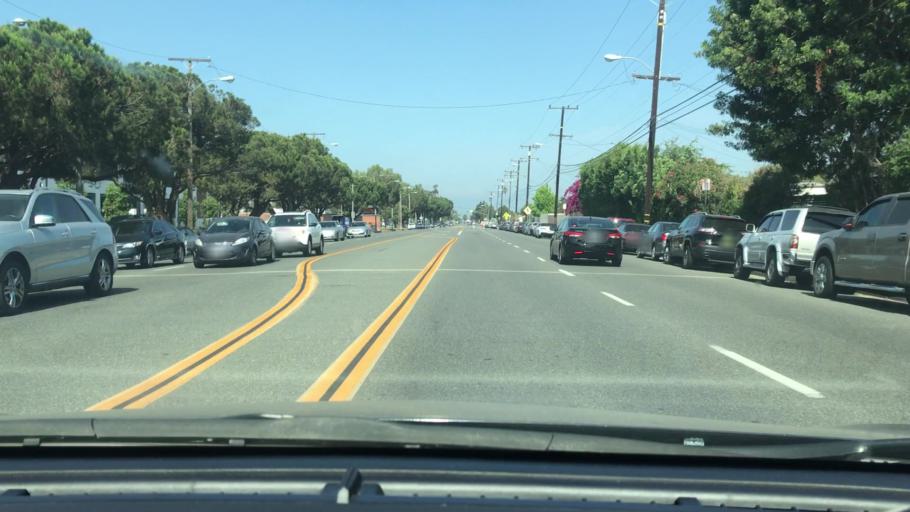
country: US
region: California
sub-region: Los Angeles County
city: Alondra Park
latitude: 33.8874
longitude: -118.3312
